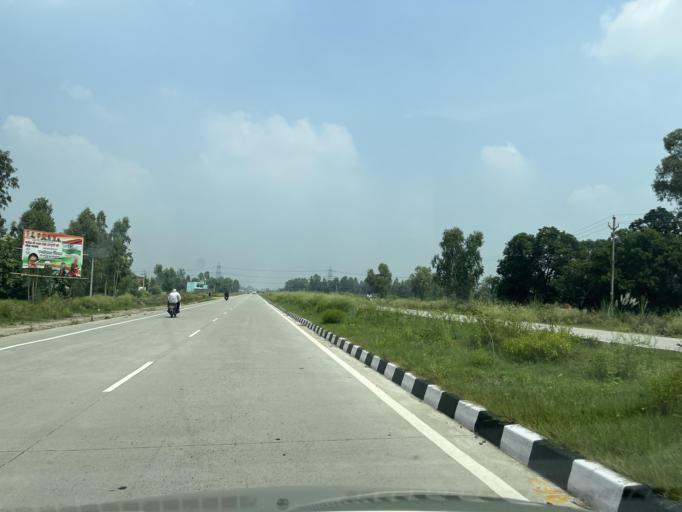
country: IN
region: Uttar Pradesh
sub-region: Bijnor
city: Najibabad
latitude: 29.5548
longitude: 78.3391
